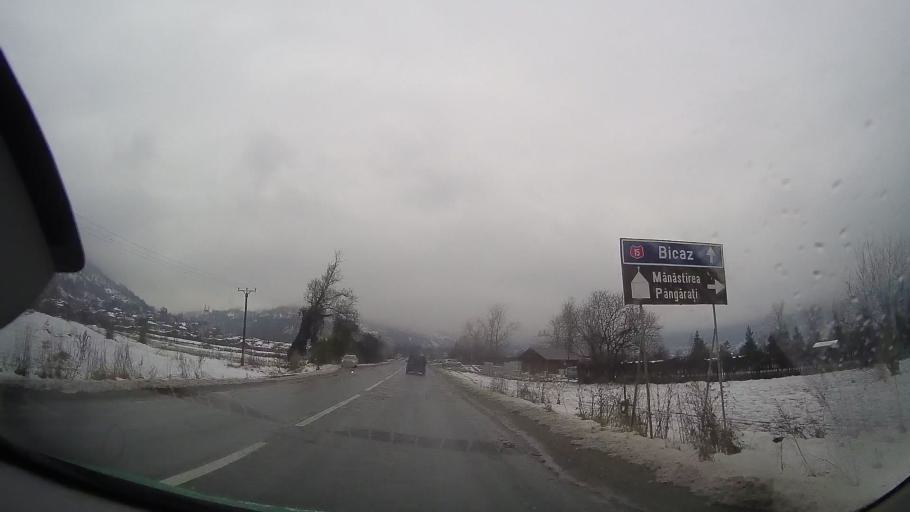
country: RO
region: Neamt
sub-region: Comuna Pangarati
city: Stejaru
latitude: 46.9218
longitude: 26.1894
